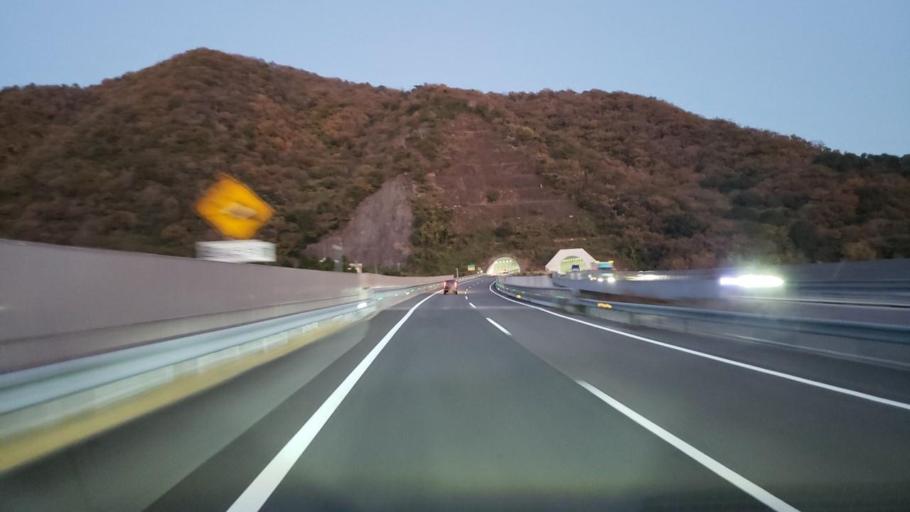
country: JP
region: Tokushima
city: Narutocho-mitsuishi
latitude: 34.1661
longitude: 134.5392
